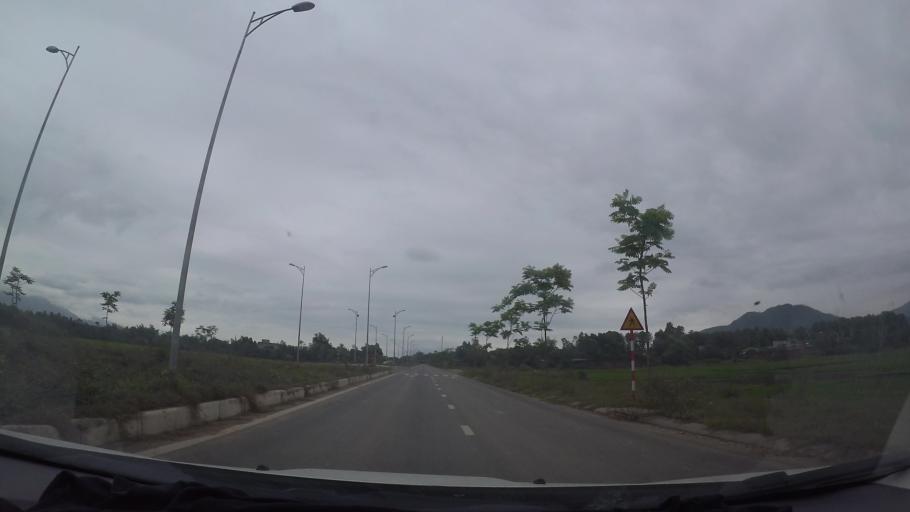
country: VN
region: Da Nang
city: Lien Chieu
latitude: 16.0763
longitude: 108.0922
